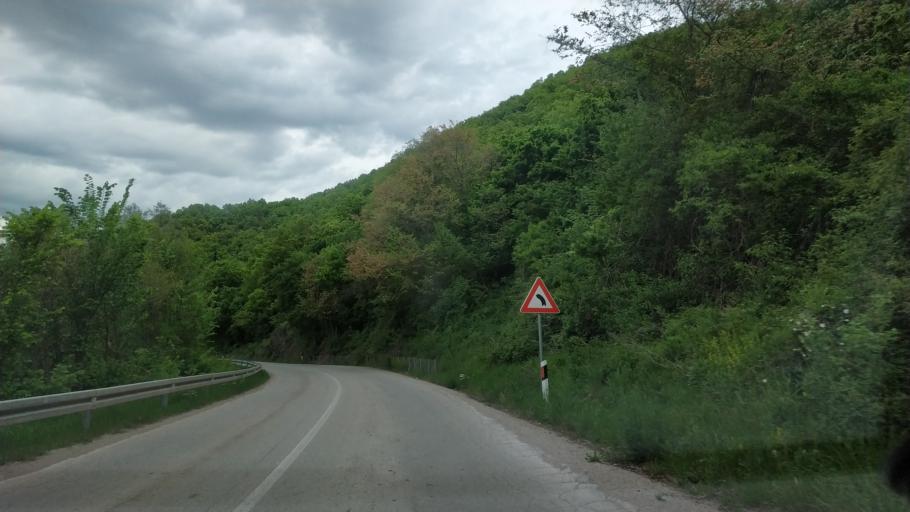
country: RS
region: Central Serbia
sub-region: Nisavski Okrug
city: Aleksinac
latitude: 43.6235
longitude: 21.6956
